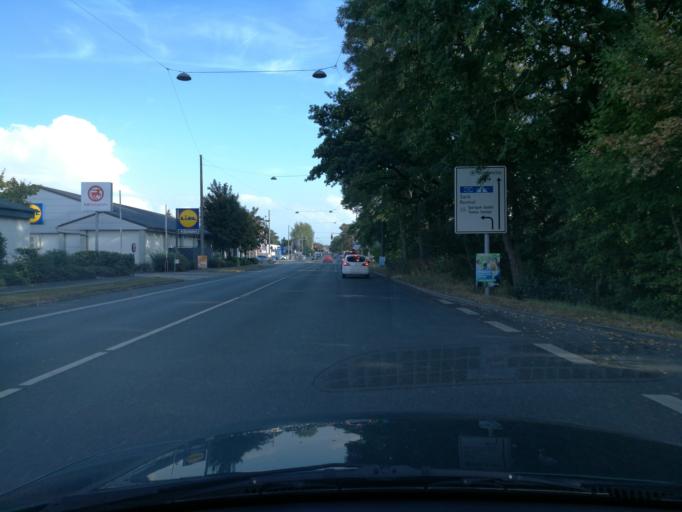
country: DE
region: Bavaria
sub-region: Regierungsbezirk Mittelfranken
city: Furth
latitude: 49.4937
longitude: 10.9887
